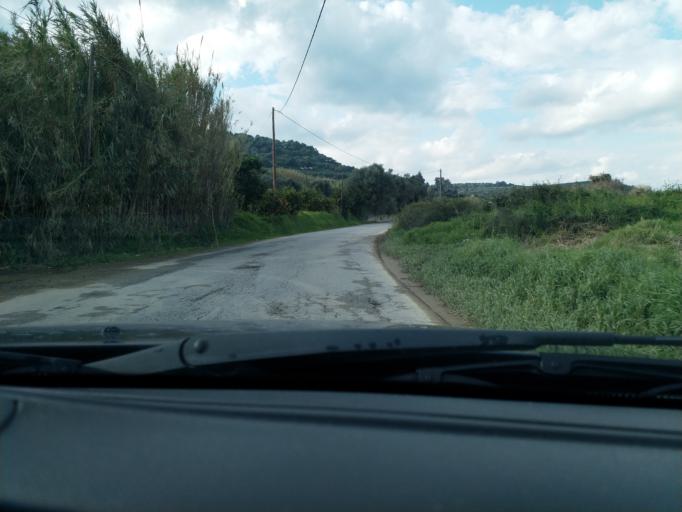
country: GR
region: Crete
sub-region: Nomos Chanias
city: Gerani
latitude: 35.4991
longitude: 23.9005
